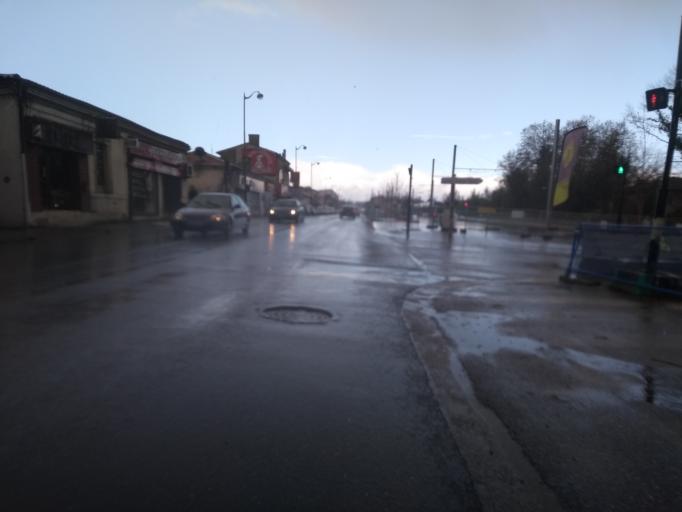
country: FR
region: Aquitaine
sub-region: Departement de la Gironde
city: Villenave-d'Ornon
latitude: 44.7856
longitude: -0.5664
